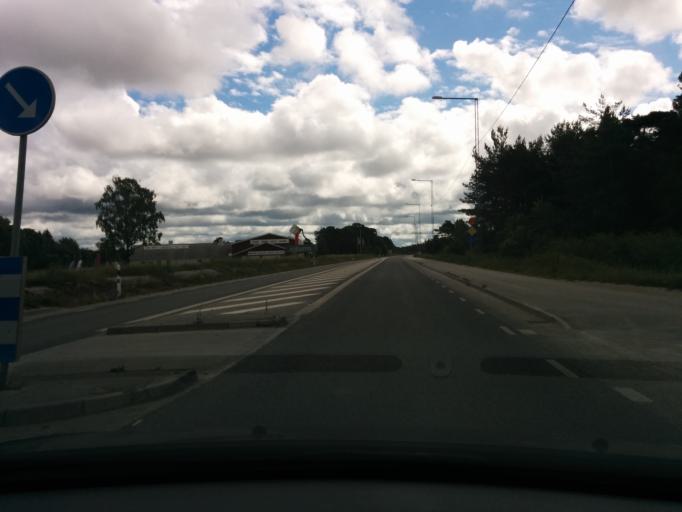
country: SE
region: Gotland
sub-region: Gotland
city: Visby
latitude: 57.6316
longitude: 18.3341
